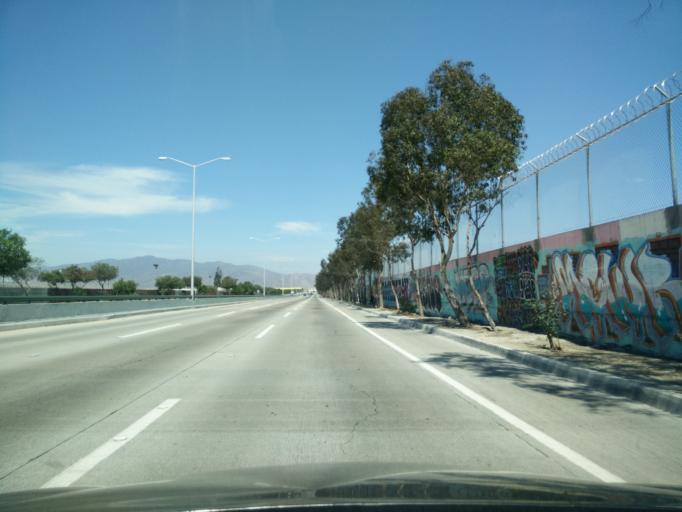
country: MX
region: Baja California
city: Tijuana
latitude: 32.5458
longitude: -116.9883
